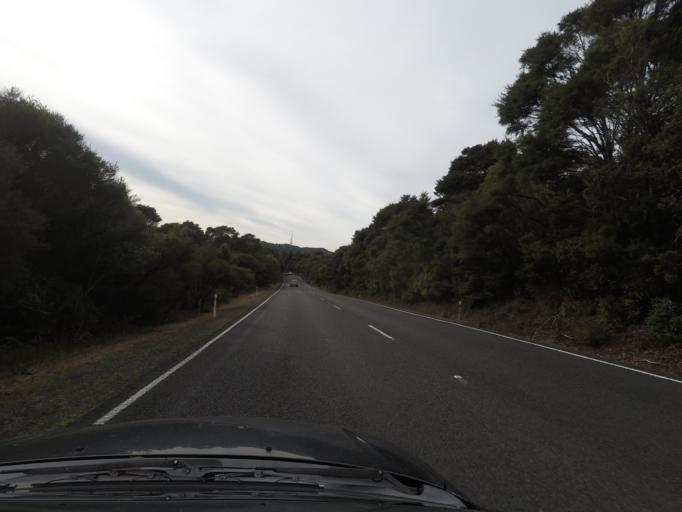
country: NZ
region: Auckland
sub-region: Auckland
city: Titirangi
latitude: -36.9415
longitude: 174.5530
